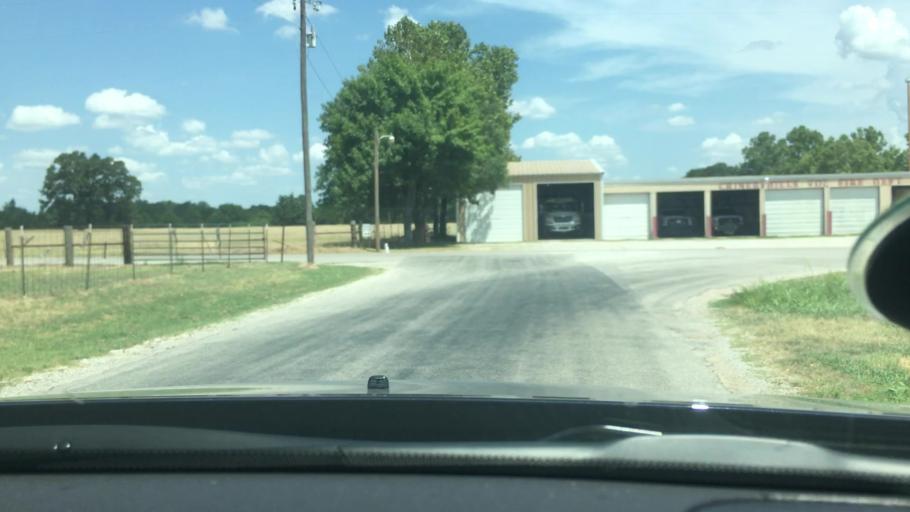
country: US
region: Oklahoma
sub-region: Carter County
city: Ardmore
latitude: 34.0707
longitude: -97.1957
